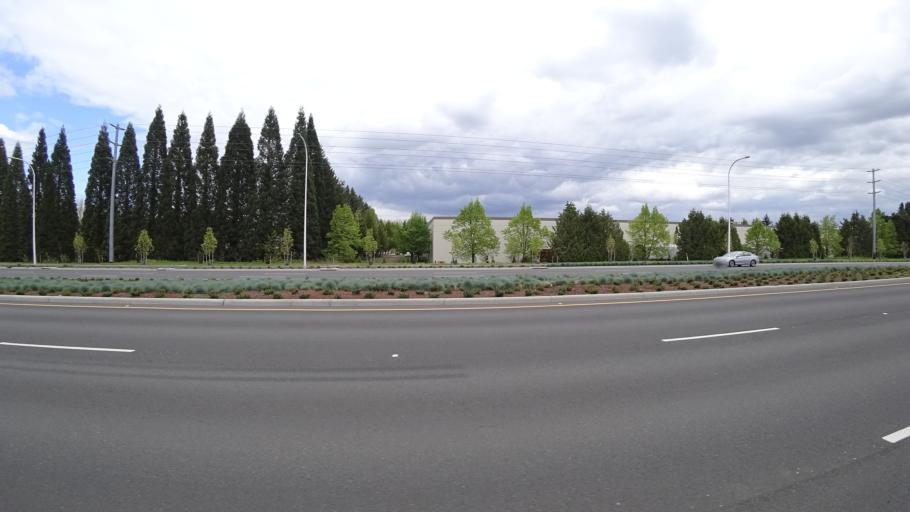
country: US
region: Oregon
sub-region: Washington County
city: Rockcreek
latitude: 45.5447
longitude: -122.9001
